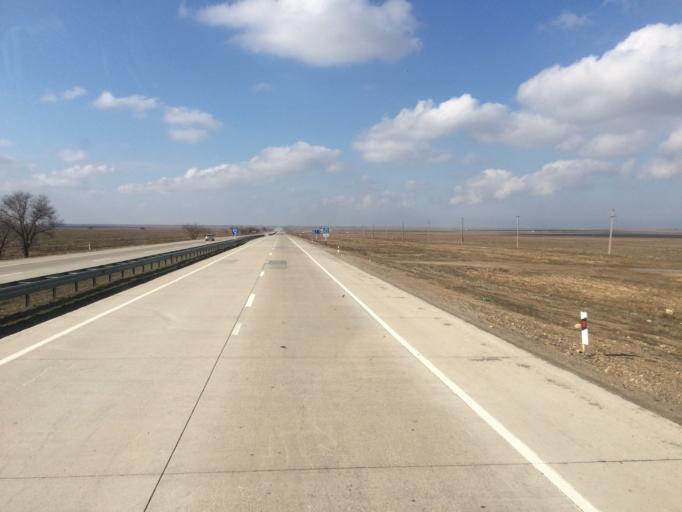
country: KZ
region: Ongtustik Qazaqstan
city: Temirlanovka
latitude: 42.8321
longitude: 69.1246
